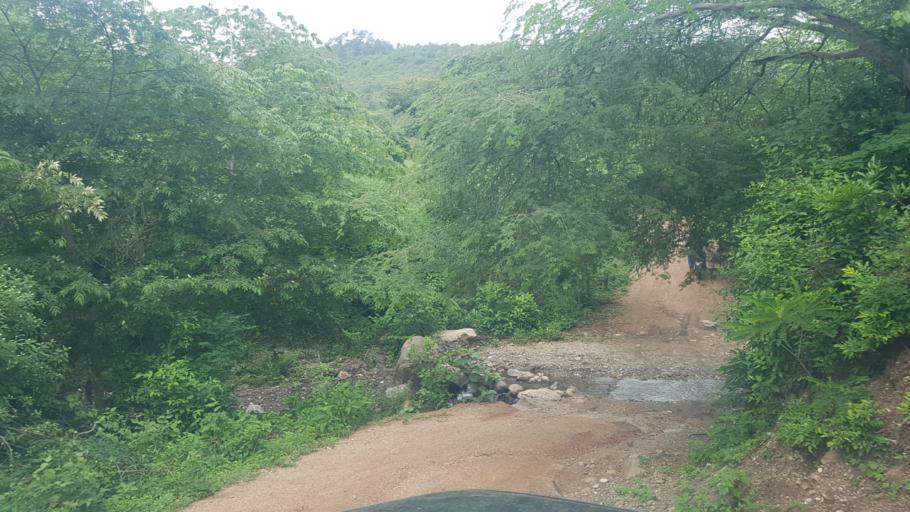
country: NI
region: Nueva Segovia
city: Ocotal
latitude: 13.6350
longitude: -86.6050
